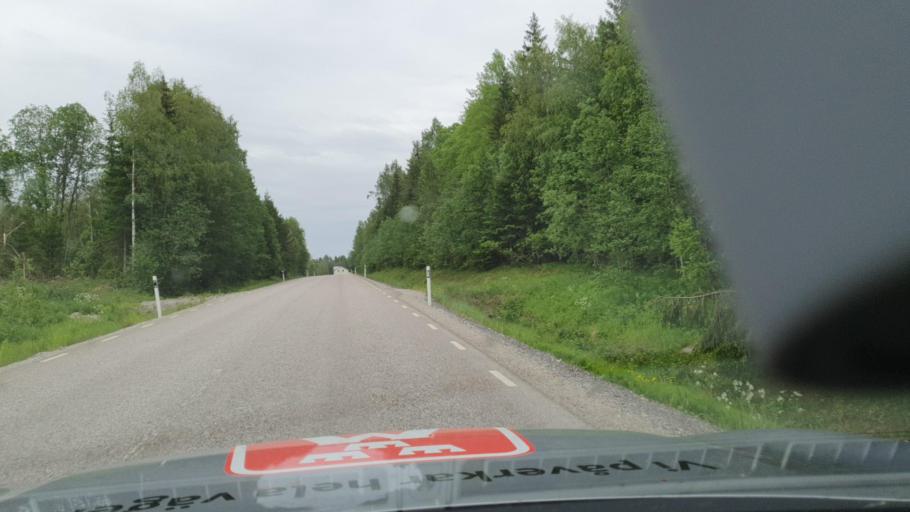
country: SE
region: Vaesternorrland
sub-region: Kramfors Kommun
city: Kramfors
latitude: 62.9205
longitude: 17.9457
